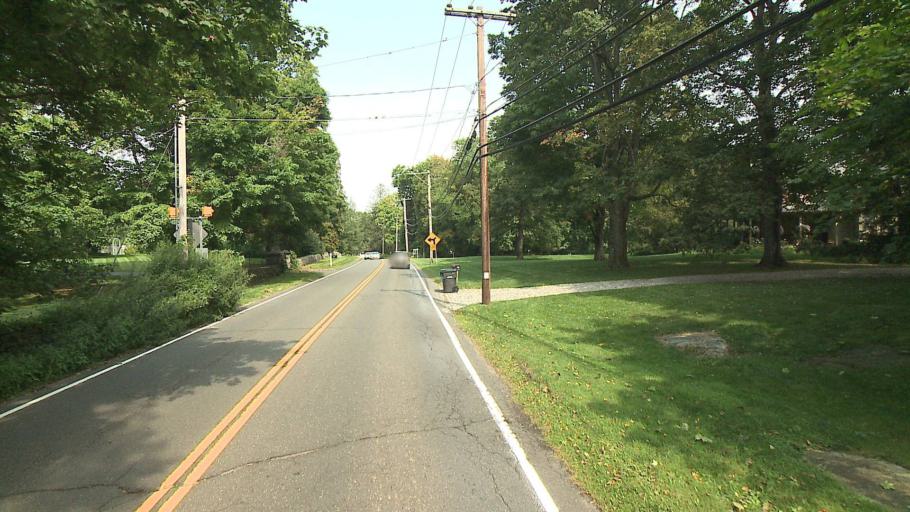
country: US
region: Connecticut
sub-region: Fairfield County
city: Ridgefield
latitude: 41.2740
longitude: -73.4884
